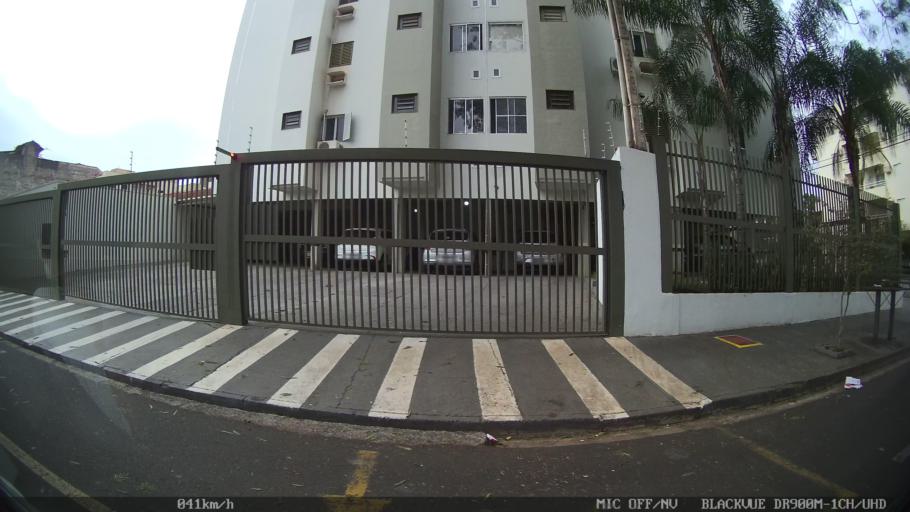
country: BR
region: Sao Paulo
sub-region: Sao Jose Do Rio Preto
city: Sao Jose do Rio Preto
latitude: -20.8339
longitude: -49.3885
